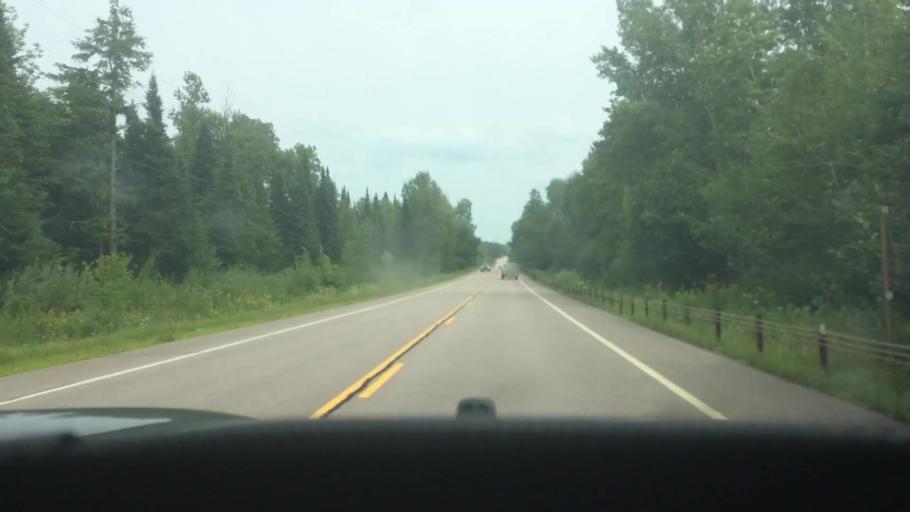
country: US
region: New York
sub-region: Franklin County
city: Malone
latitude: 44.8545
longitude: -74.0658
